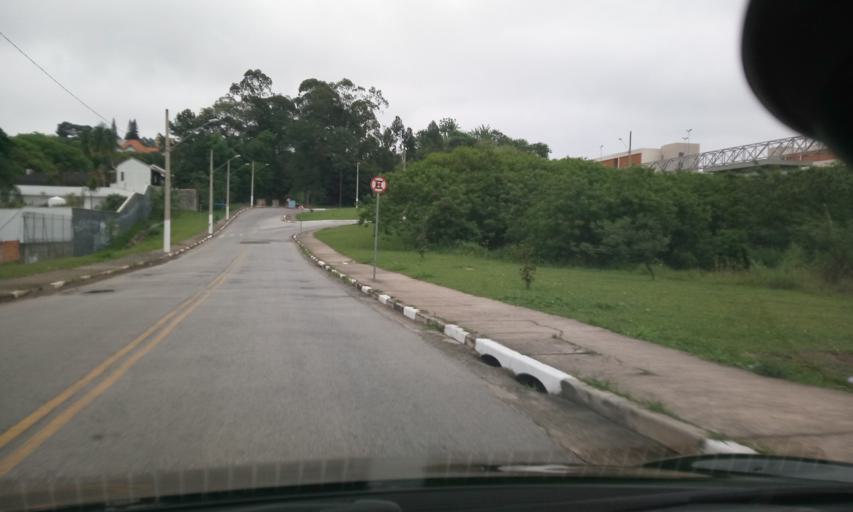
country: BR
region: Sao Paulo
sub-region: Sao Bernardo Do Campo
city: Sao Bernardo do Campo
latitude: -23.6792
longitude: -46.5623
